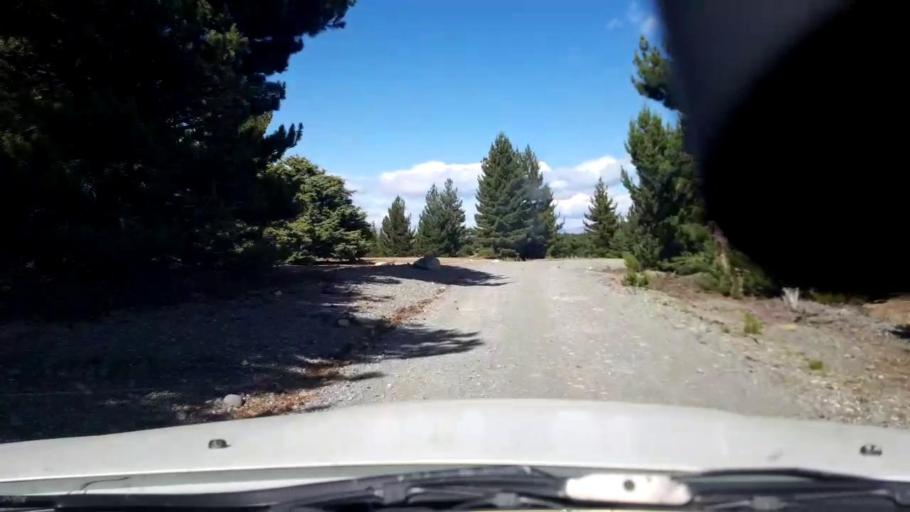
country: NZ
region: Canterbury
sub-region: Timaru District
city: Pleasant Point
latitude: -44.0148
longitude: 170.4719
